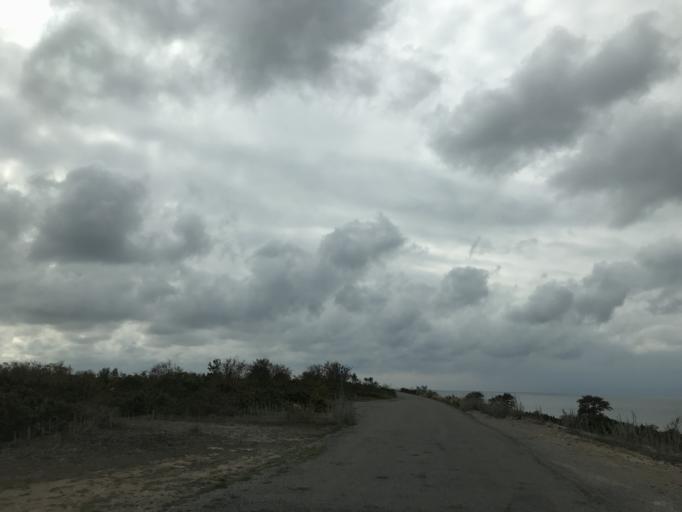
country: SE
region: Kalmar
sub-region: Borgholms Kommun
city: Borgholm
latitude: 57.0444
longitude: 16.8293
